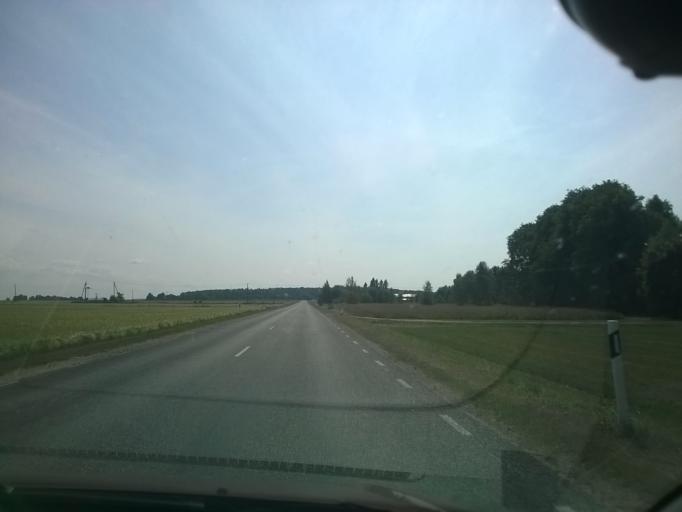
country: EE
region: Tartu
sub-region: Puhja vald
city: Puhja
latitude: 58.2665
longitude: 26.1760
